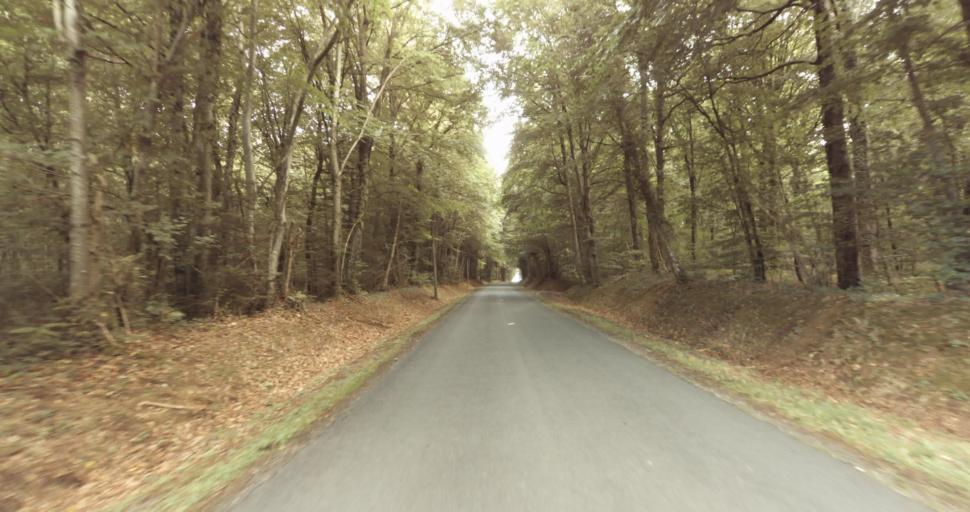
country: FR
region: Lower Normandy
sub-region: Departement de l'Orne
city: Gace
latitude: 48.8215
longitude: 0.2347
